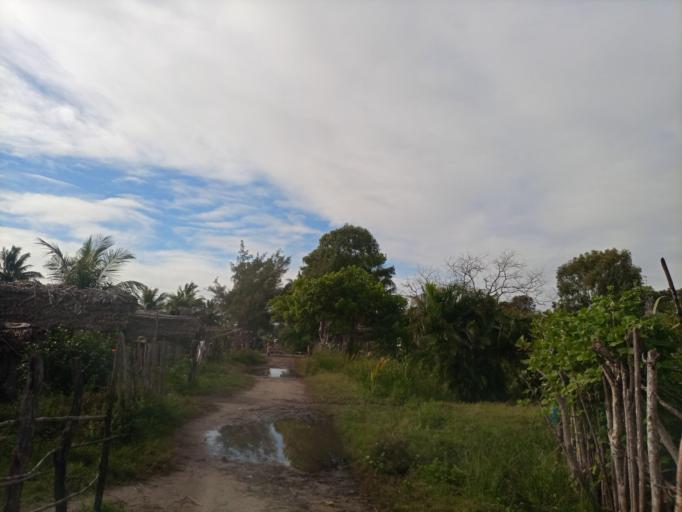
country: MG
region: Anosy
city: Fort Dauphin
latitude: -24.7797
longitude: 47.1905
